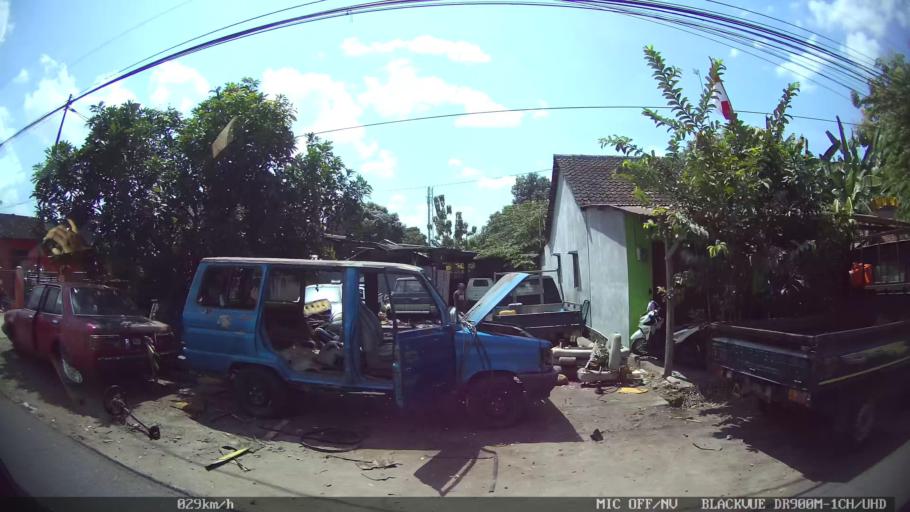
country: ID
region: Daerah Istimewa Yogyakarta
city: Sewon
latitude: -7.8397
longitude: 110.3818
